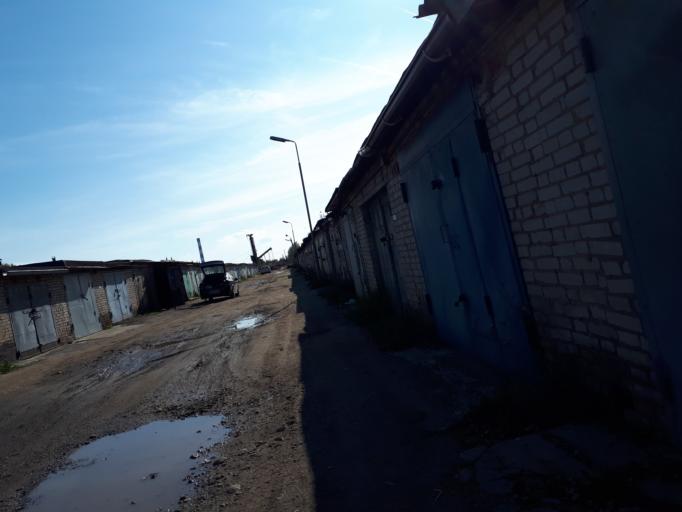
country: BY
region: Vitebsk
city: Vitebsk
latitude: 55.1691
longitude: 30.2459
